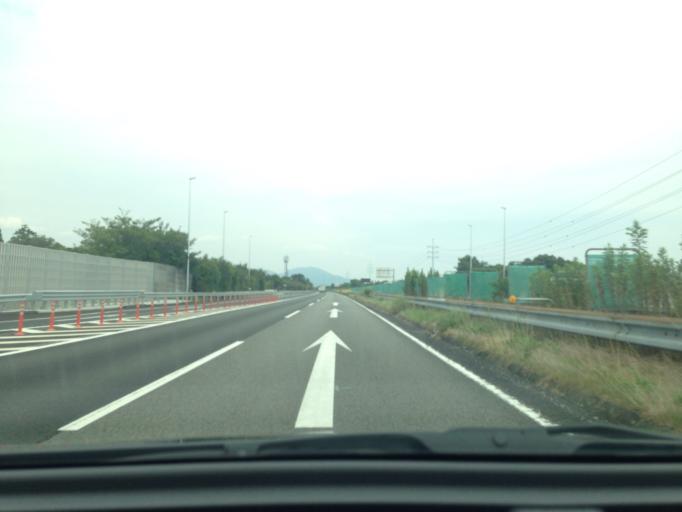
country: JP
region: Shizuoka
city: Fujieda
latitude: 34.8198
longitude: 138.2674
